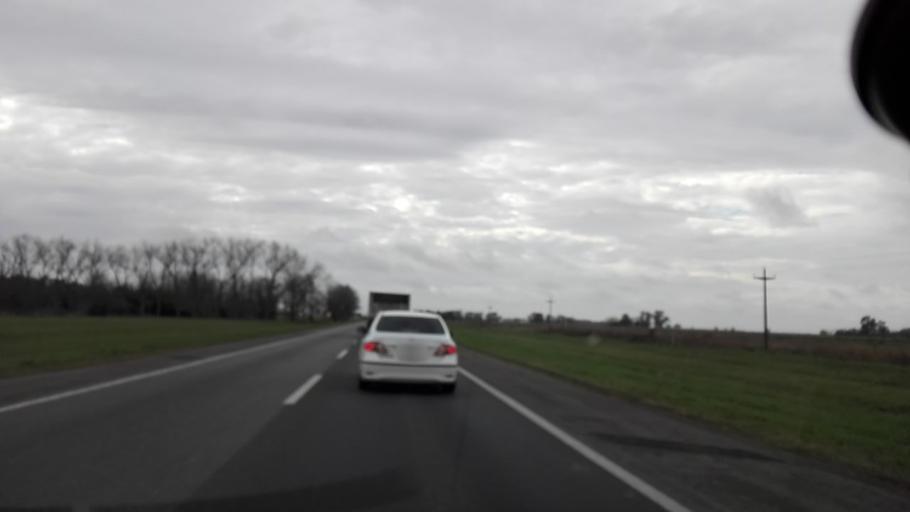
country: AR
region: Buenos Aires
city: San Miguel del Monte
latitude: -35.6213
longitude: -58.8345
